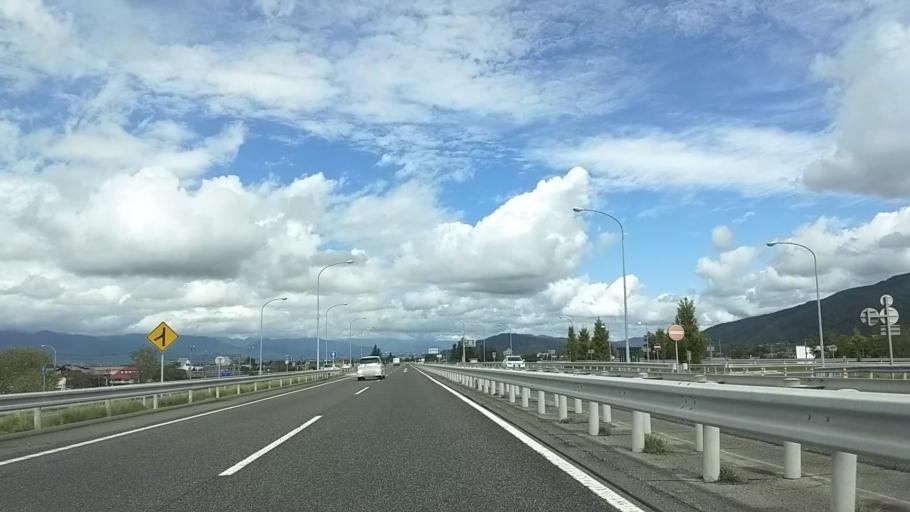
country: JP
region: Nagano
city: Toyoshina
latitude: 36.2978
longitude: 137.9258
